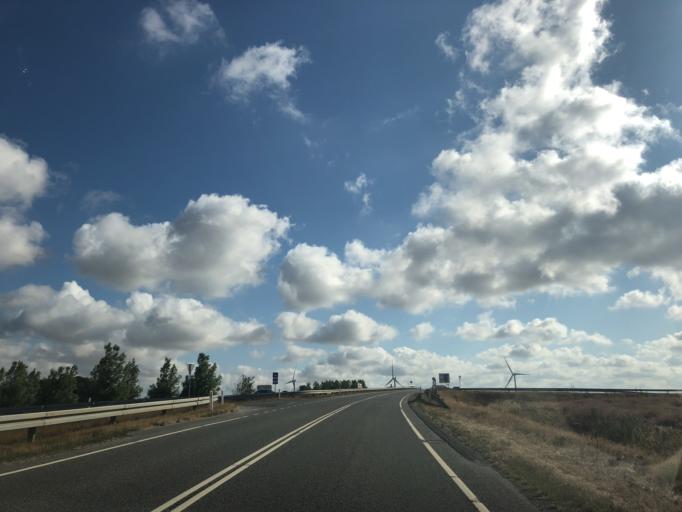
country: DK
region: Central Jutland
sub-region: Skive Kommune
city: Skive
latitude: 56.6707
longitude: 8.9527
